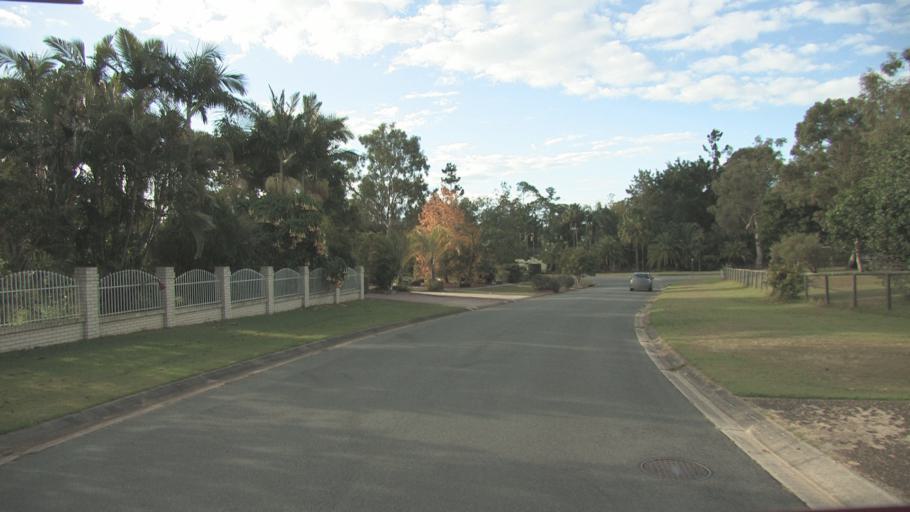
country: AU
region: Queensland
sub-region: Logan
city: Park Ridge South
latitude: -27.7055
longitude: 153.0240
